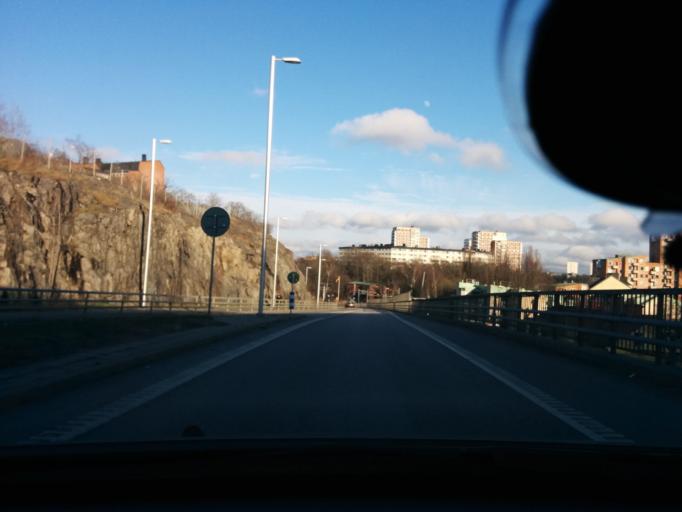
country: SE
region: Stockholm
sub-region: Solna Kommun
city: Solna
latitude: 59.3156
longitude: 18.0028
